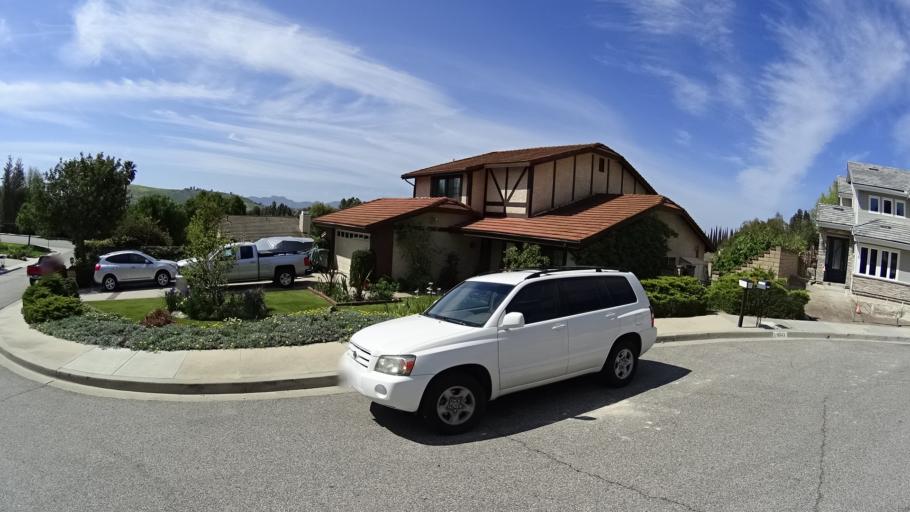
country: US
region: California
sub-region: Ventura County
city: Thousand Oaks
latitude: 34.2207
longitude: -118.8375
